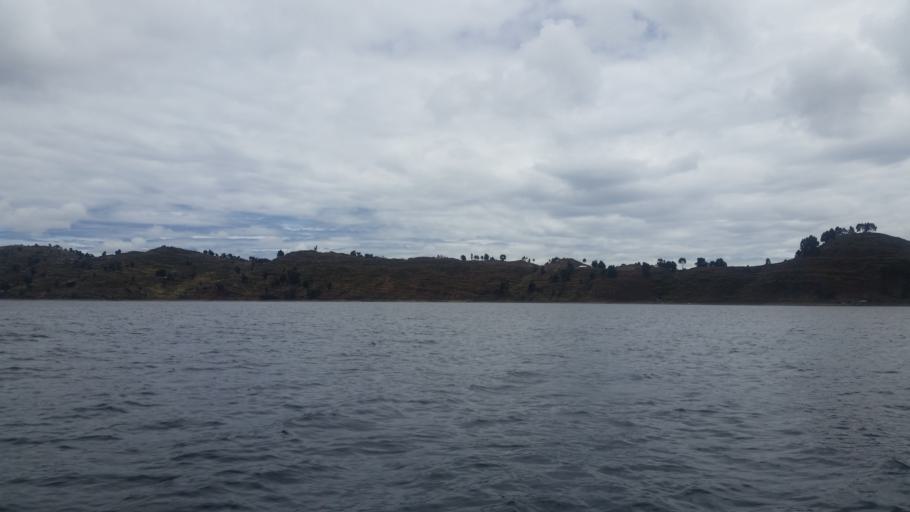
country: PE
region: Puno
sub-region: Provincia de Puno
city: Taquile
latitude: -15.7953
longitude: -69.6914
